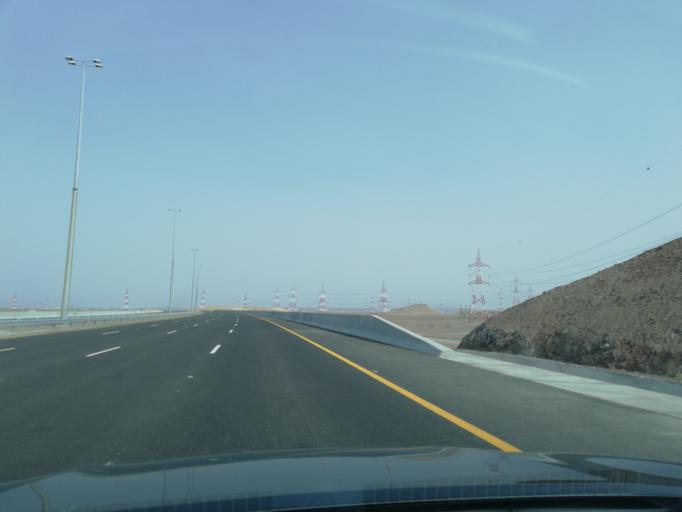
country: OM
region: Al Batinah
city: Al Sohar
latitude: 24.3327
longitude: 56.5570
